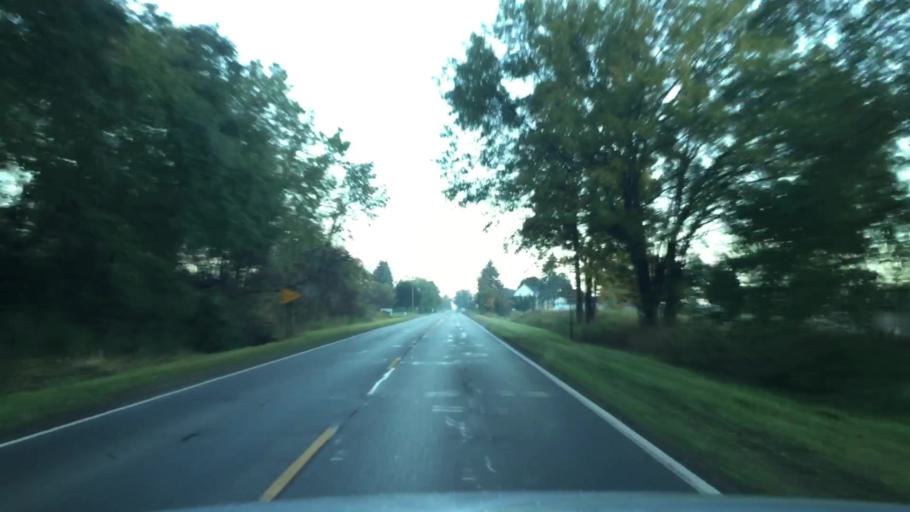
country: US
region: Michigan
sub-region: Livingston County
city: Howell
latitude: 42.6591
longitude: -83.9356
